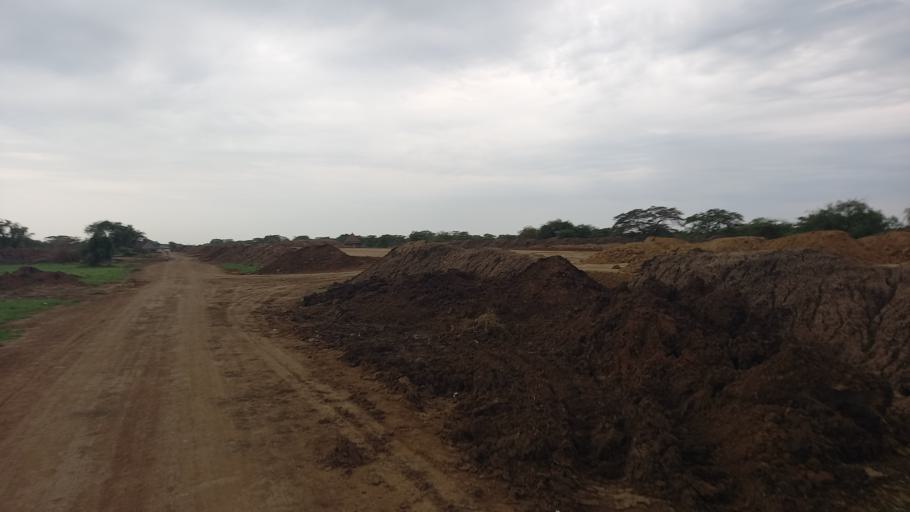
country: ET
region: Gambela
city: Gambela
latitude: 8.3340
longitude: 33.9469
